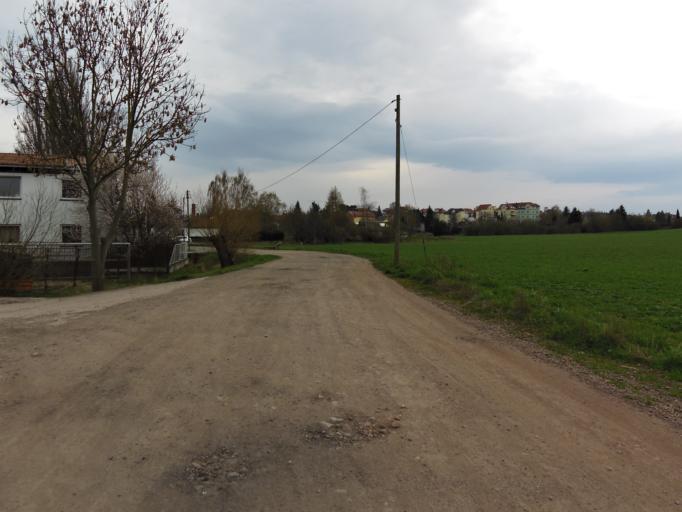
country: DE
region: Thuringia
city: Gotha
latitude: 50.9577
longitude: 10.7061
